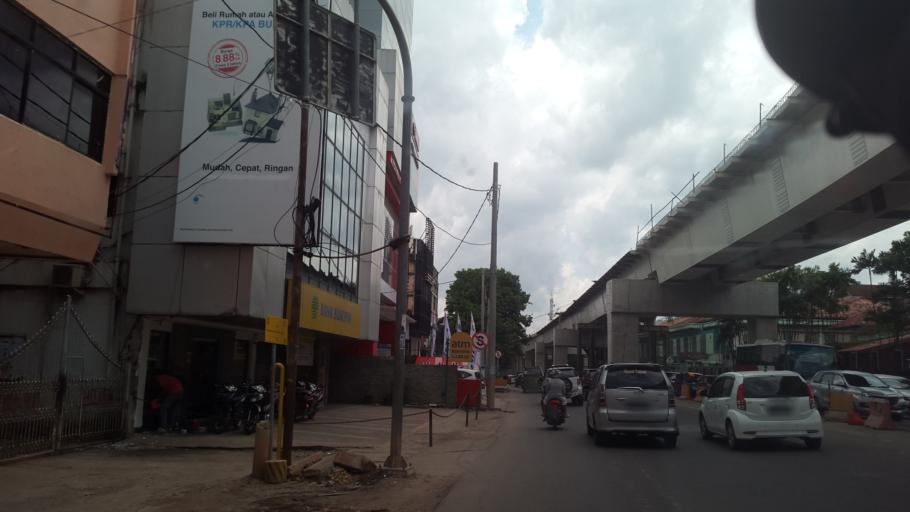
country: ID
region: South Sumatra
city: Plaju
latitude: -2.9771
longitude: 104.7538
